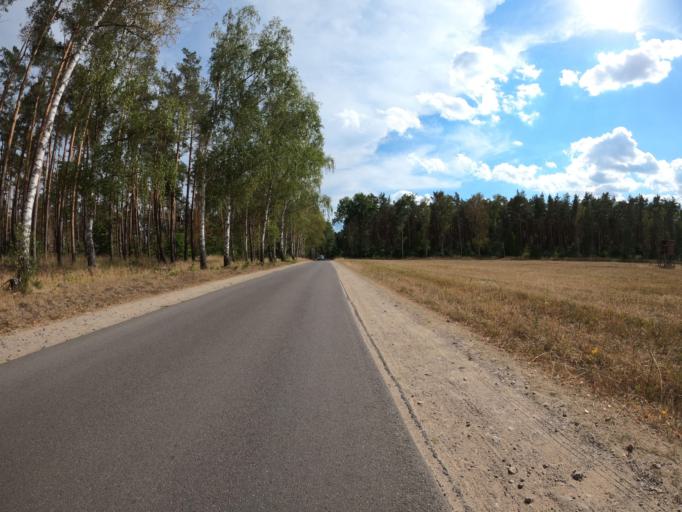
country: DE
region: Brandenburg
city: Lychen
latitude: 53.2904
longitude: 13.4283
